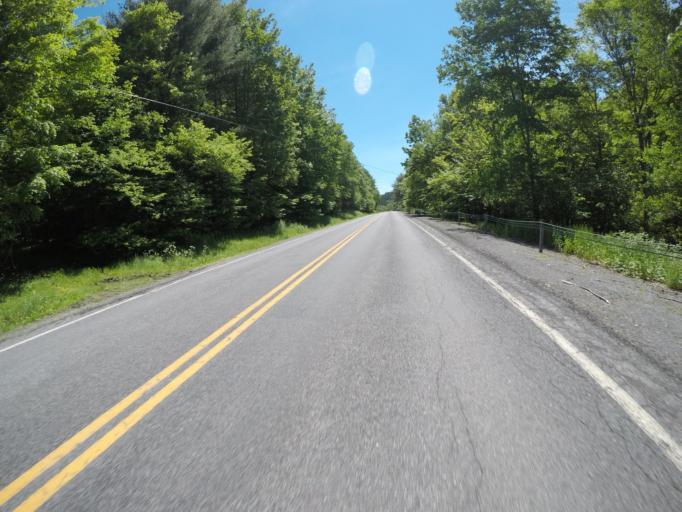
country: US
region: New York
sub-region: Delaware County
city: Delhi
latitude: 42.2166
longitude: -74.8821
